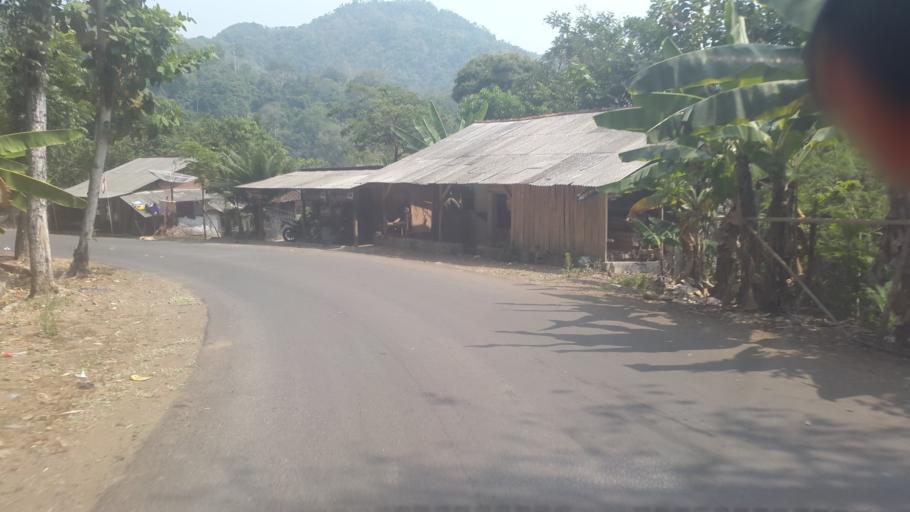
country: ID
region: West Java
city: Tugu
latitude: -6.9359
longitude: 106.4560
